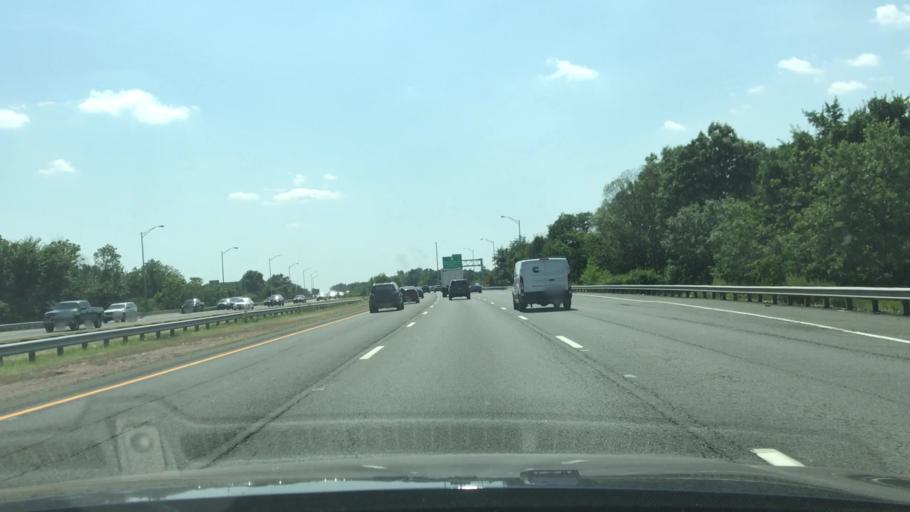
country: US
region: New Jersey
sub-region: Middlesex County
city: Middlesex
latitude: 40.5549
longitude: -74.4816
